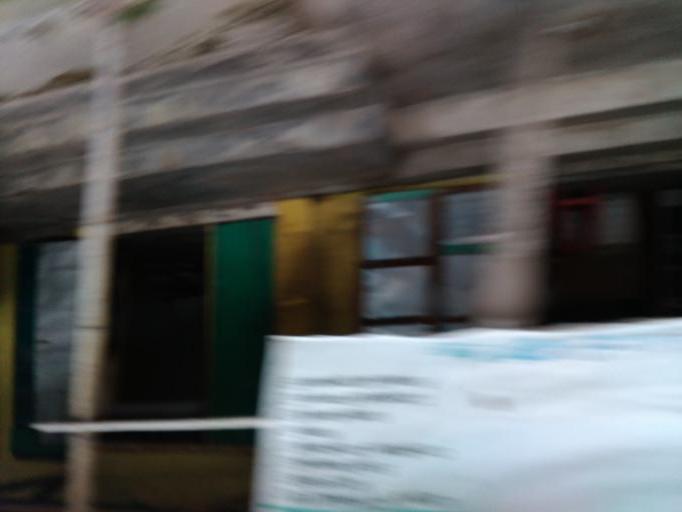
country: ID
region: Central Java
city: Boyolali
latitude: -7.5272
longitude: 110.5990
